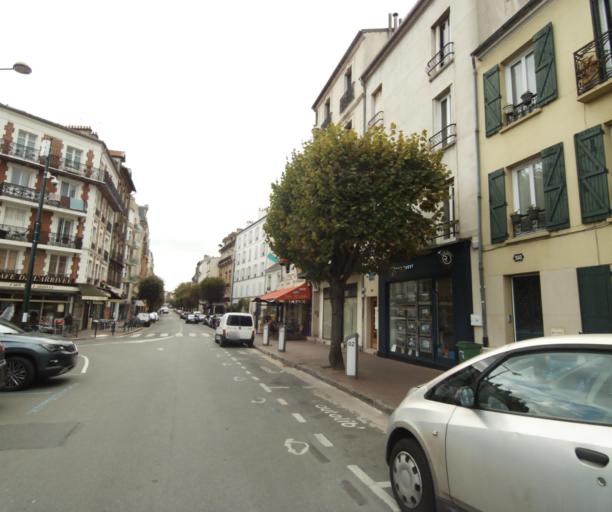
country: FR
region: Ile-de-France
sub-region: Departement des Hauts-de-Seine
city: Issy-les-Moulineaux
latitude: 48.8136
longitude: 2.2721
